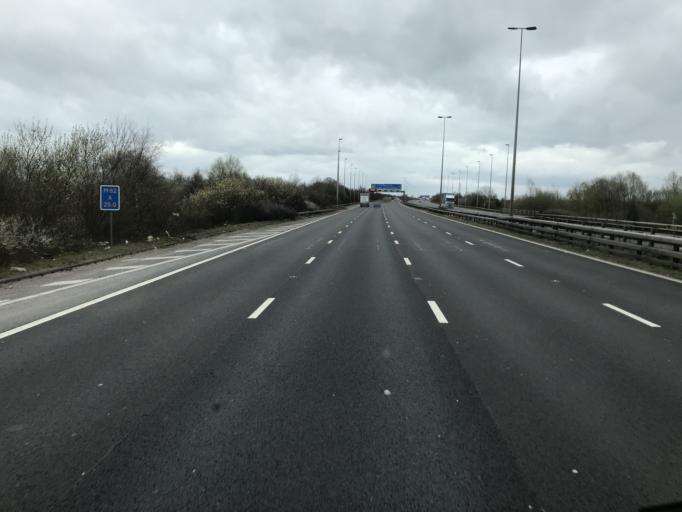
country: GB
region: England
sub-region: Warrington
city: Winwick
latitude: 53.4193
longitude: -2.6229
